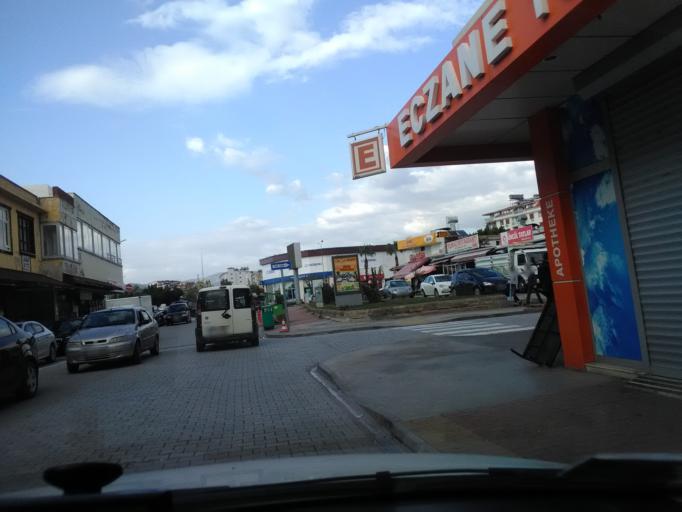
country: TR
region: Antalya
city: Gazipasa
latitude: 36.2689
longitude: 32.3175
